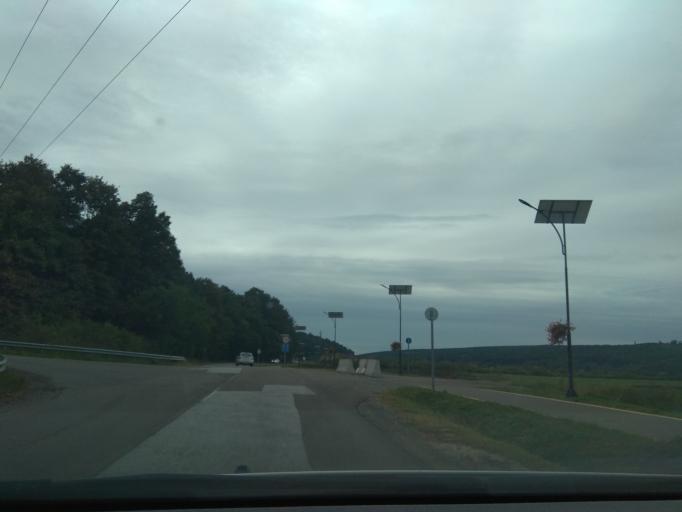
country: HU
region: Heves
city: Egerszalok
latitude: 47.8589
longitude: 20.3294
